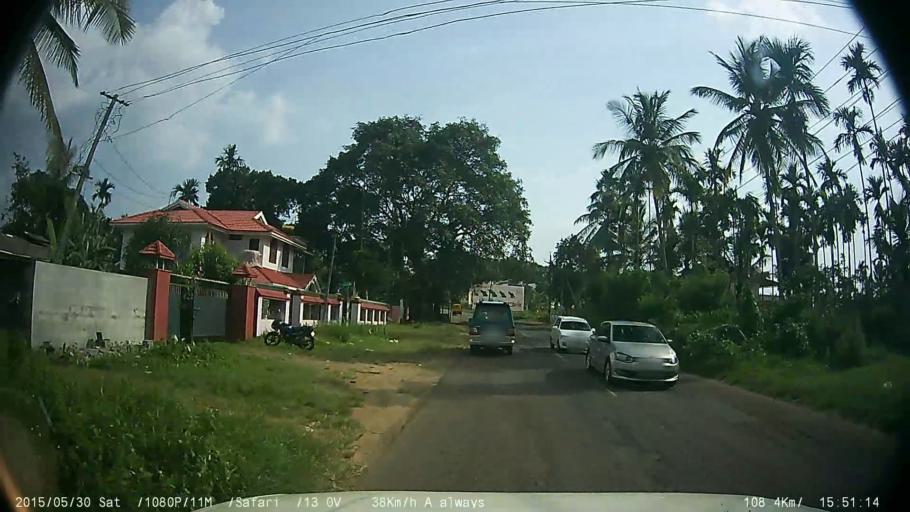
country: IN
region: Kerala
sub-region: Wayanad
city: Panamaram
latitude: 11.6823
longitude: 76.0757
